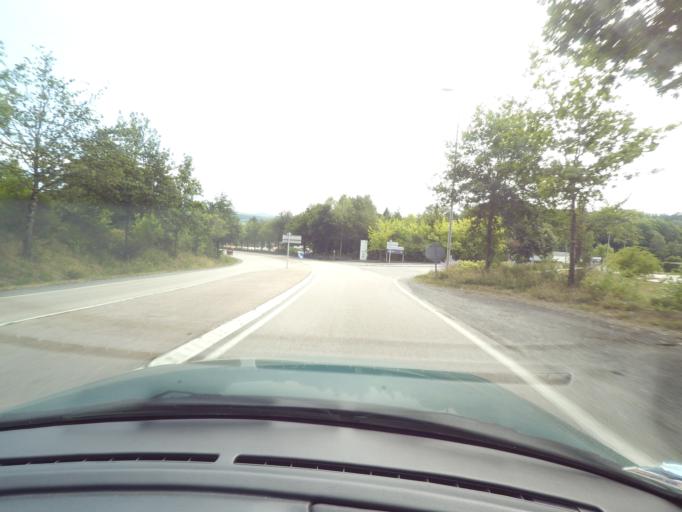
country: FR
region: Limousin
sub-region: Departement de la Haute-Vienne
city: Eymoutiers
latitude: 45.7388
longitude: 1.7317
